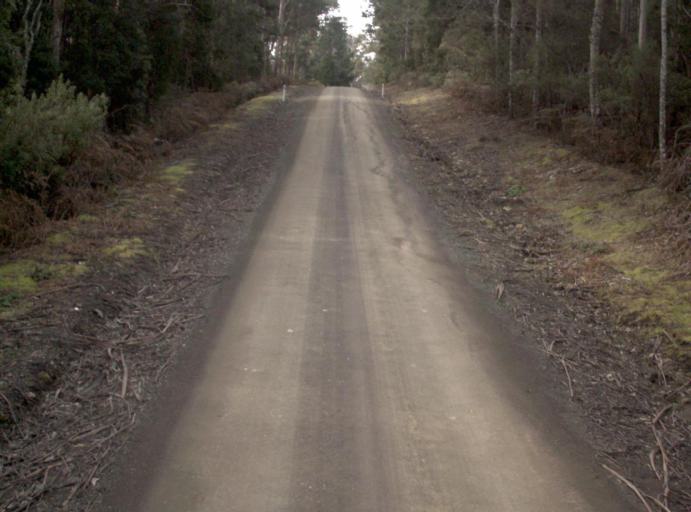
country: AU
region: Tasmania
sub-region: Dorset
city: Scottsdale
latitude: -41.2770
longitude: 147.3423
